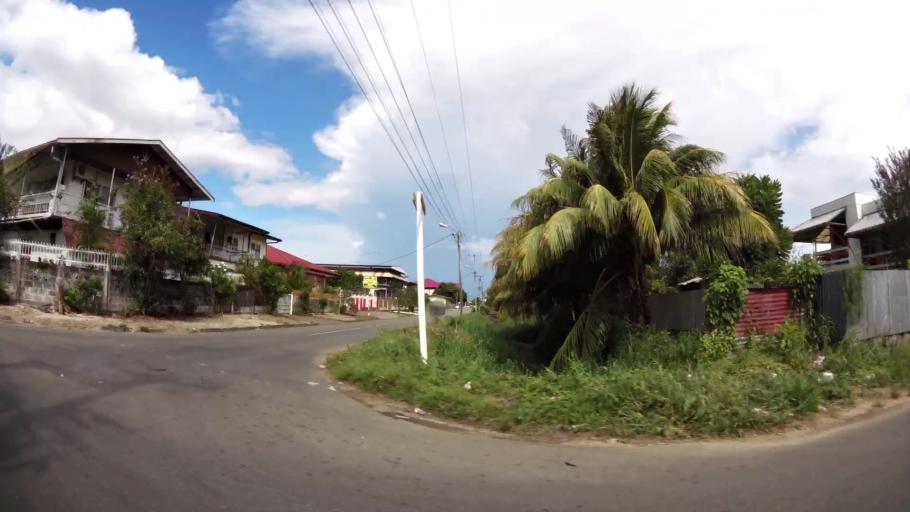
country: SR
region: Paramaribo
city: Paramaribo
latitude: 5.8400
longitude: -55.1484
